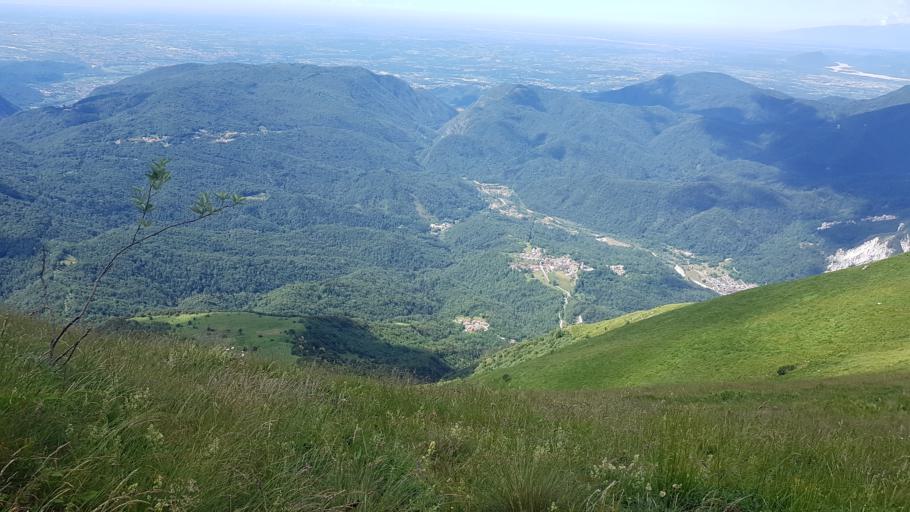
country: IT
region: Friuli Venezia Giulia
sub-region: Provincia di Udine
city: Lusevera
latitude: 46.2913
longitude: 13.2965
